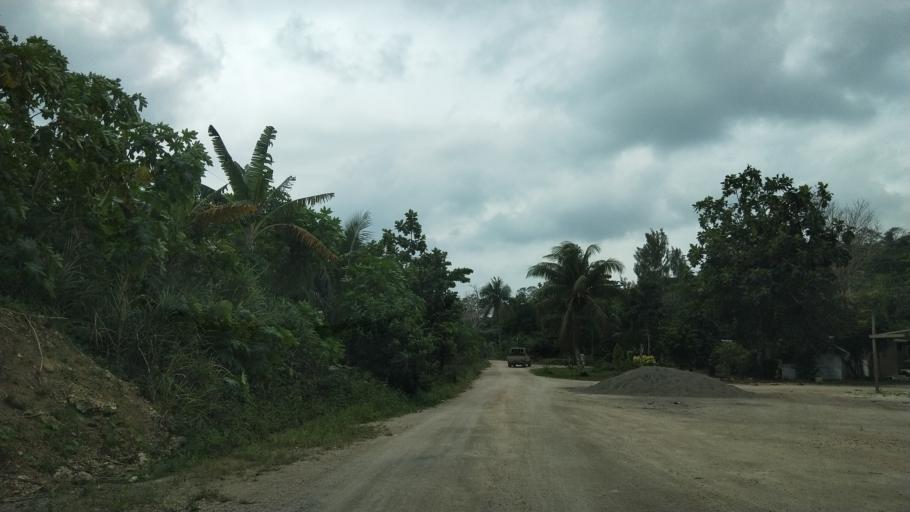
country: VU
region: Shefa
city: Port-Vila
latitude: -17.7859
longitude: 168.3591
